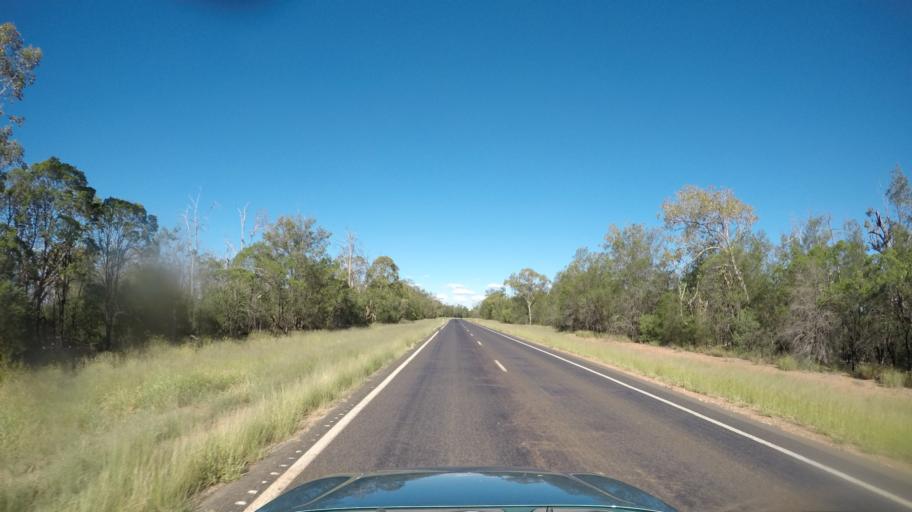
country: AU
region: Queensland
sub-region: Goondiwindi
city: Goondiwindi
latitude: -28.1595
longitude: 150.6347
